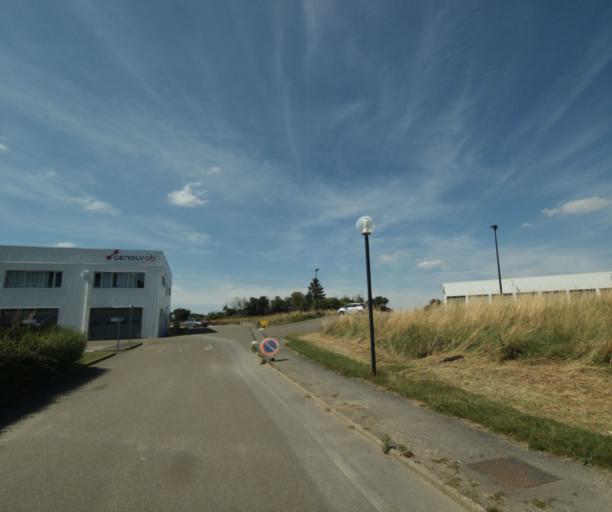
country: FR
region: Pays de la Loire
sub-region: Departement de la Mayenne
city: Change
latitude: 48.0802
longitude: -0.7859
